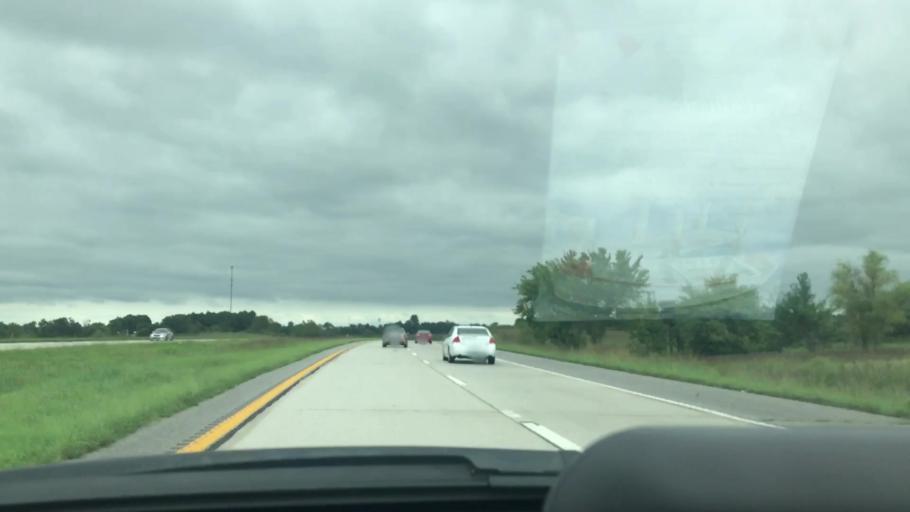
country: US
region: Missouri
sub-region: Greene County
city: Fair Grove
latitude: 37.4458
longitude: -93.1439
